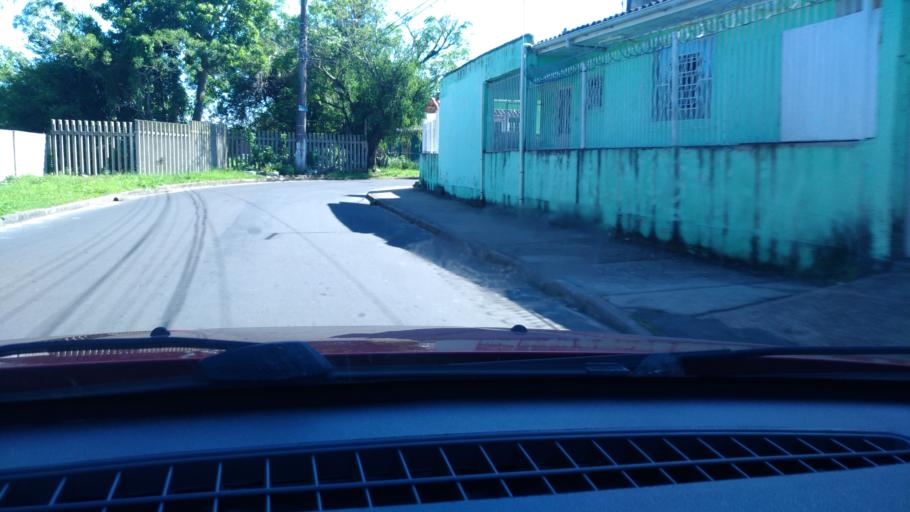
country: BR
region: Rio Grande do Sul
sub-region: Cachoeirinha
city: Cachoeirinha
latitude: -30.0344
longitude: -51.1277
